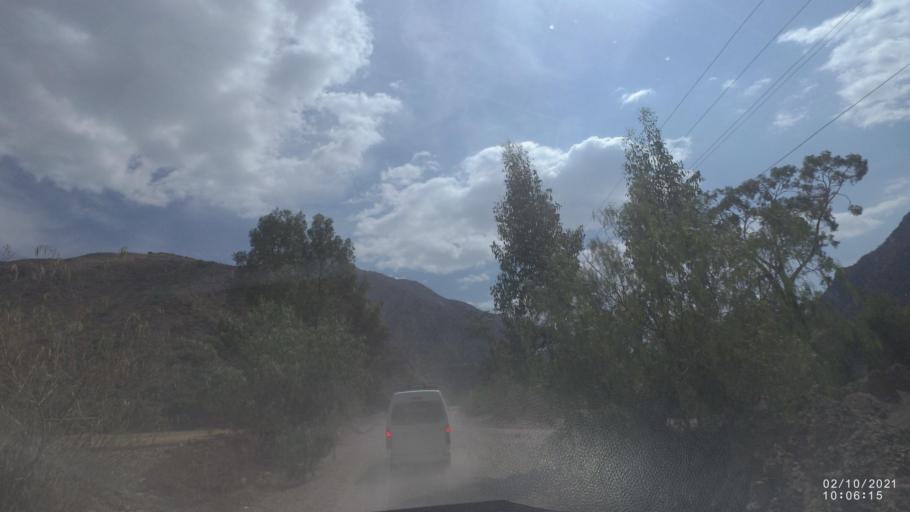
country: BO
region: Cochabamba
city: Irpa Irpa
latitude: -17.7425
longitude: -66.3524
